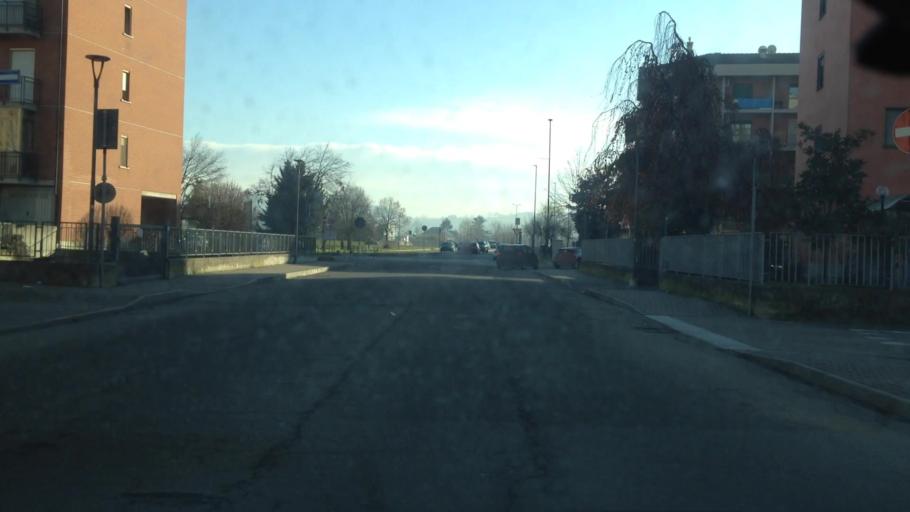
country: IT
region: Piedmont
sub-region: Provincia di Asti
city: Asti
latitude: 44.8939
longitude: 8.2182
